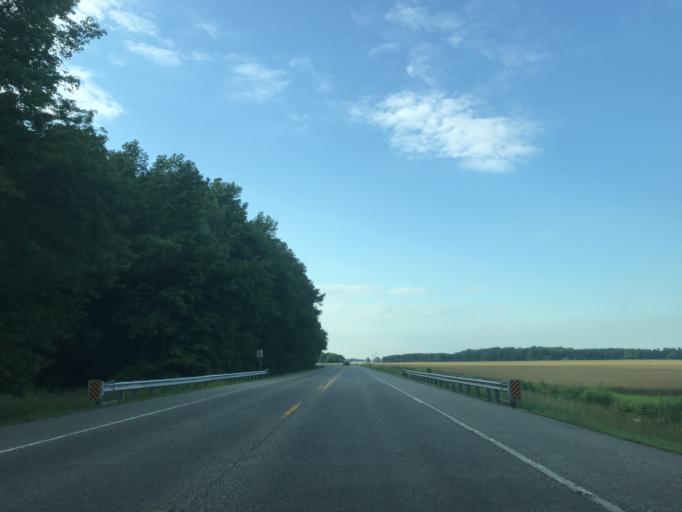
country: US
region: Maryland
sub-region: Caroline County
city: Federalsburg
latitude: 38.7923
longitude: -75.7866
